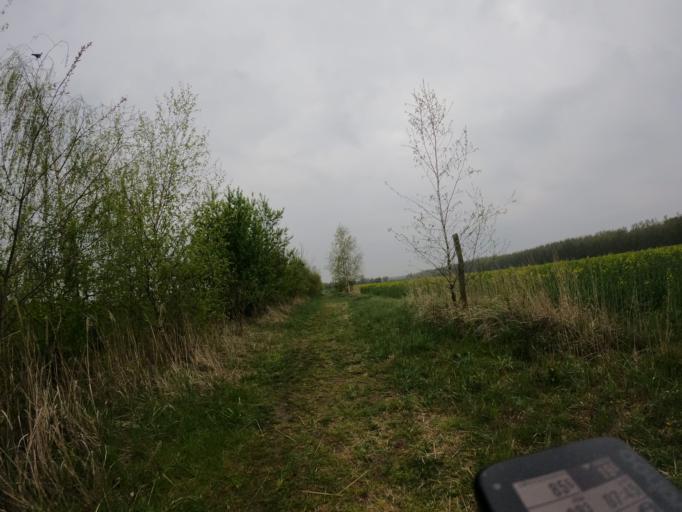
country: DE
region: Berlin
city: Lichtenrade
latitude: 52.3935
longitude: 13.4291
